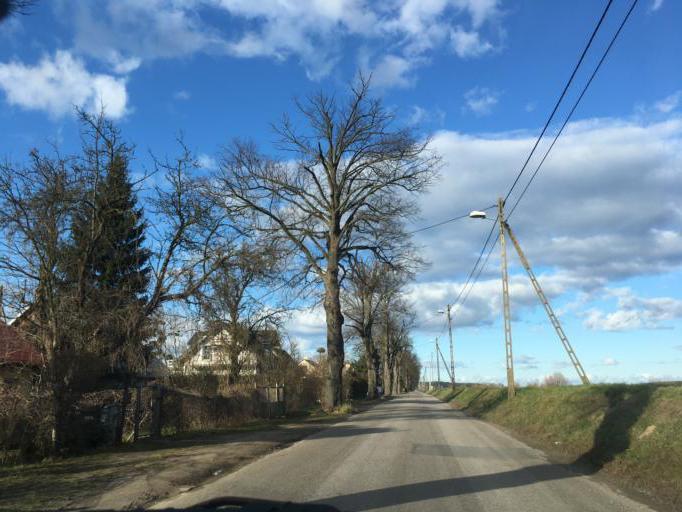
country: PL
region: Pomeranian Voivodeship
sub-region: Powiat nowodworski
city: Ostaszewo
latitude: 54.3206
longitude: 18.9315
